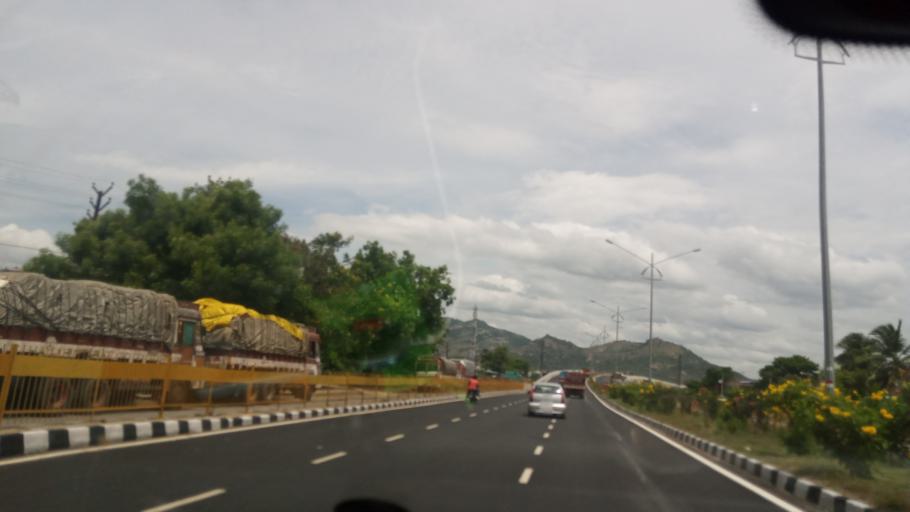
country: IN
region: Tamil Nadu
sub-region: Krishnagiri
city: Krishnagiri
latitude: 12.5194
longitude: 78.2321
